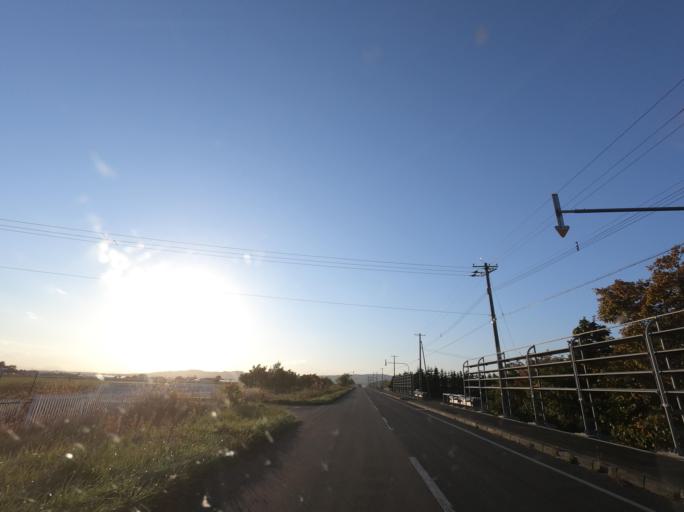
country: JP
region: Hokkaido
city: Iwamizawa
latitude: 42.9794
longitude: 141.8454
